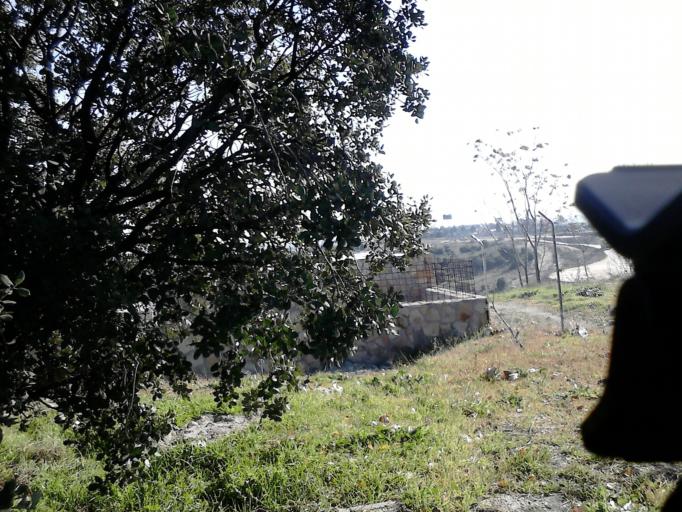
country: ES
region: Madrid
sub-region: Provincia de Madrid
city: Torrelodones
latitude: 40.5727
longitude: -3.9203
